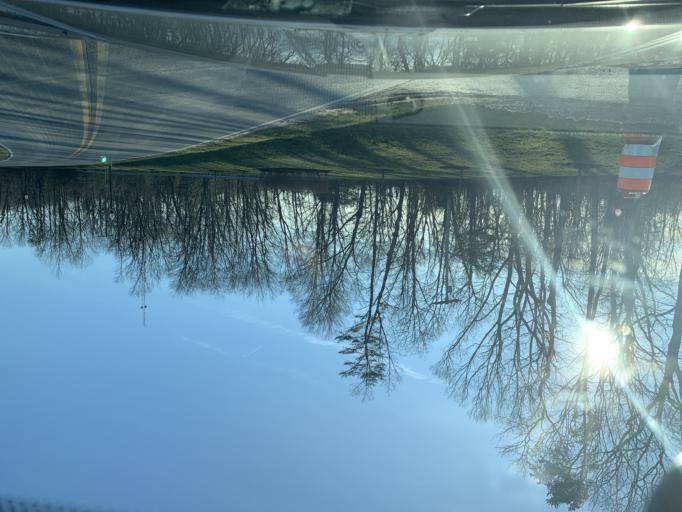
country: US
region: Maryland
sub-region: Anne Arundel County
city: Crofton
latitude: 39.0297
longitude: -76.7339
